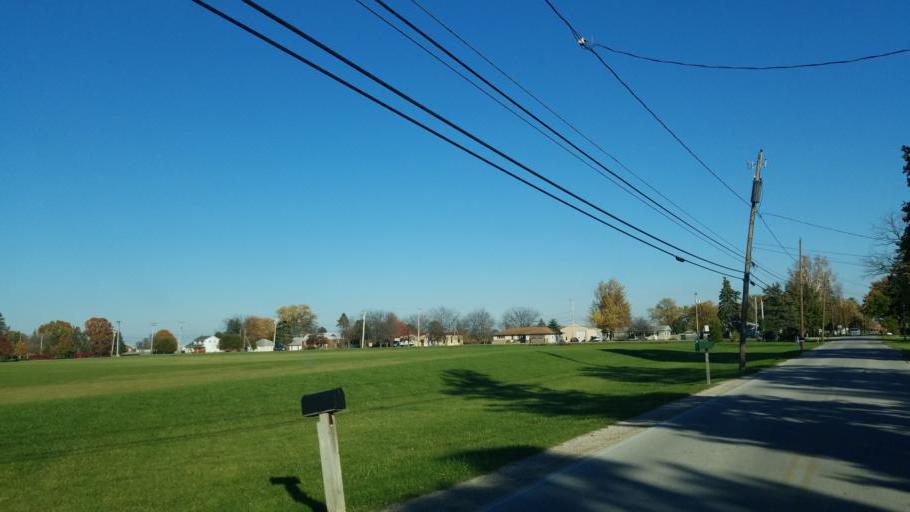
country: US
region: Ohio
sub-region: Wood County
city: Rossford
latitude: 41.5722
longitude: -83.5695
